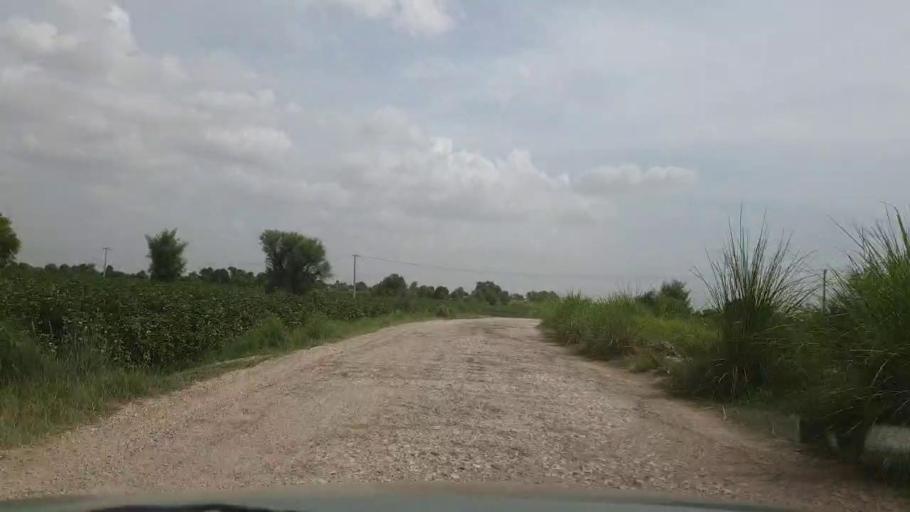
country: PK
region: Sindh
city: Kot Diji
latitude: 27.1290
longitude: 69.0284
